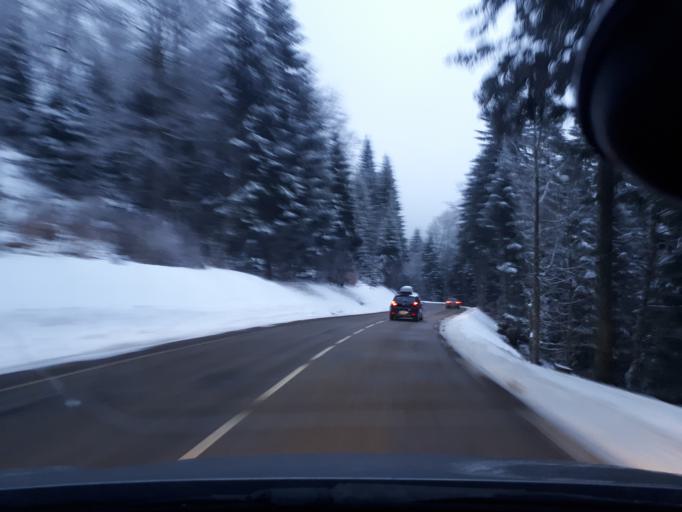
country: FR
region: Rhone-Alpes
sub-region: Departement de l'Isere
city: Vaulnaveys-le-Bas
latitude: 45.1024
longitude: 5.8509
